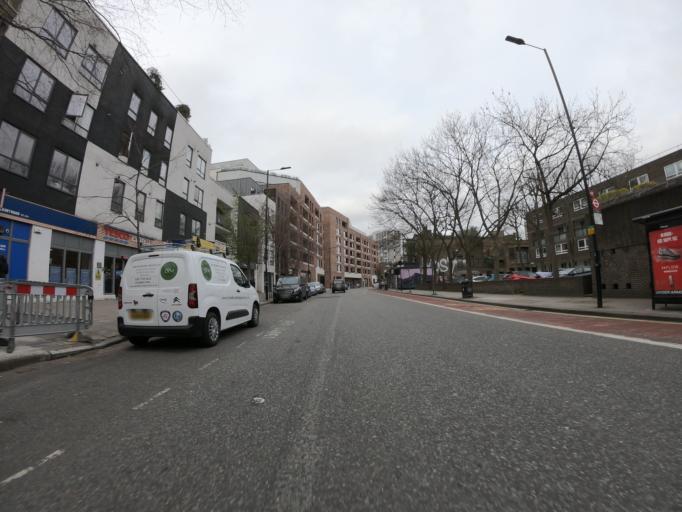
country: GB
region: England
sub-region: Greater London
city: Bethnal Green
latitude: 51.5291
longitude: -0.0751
